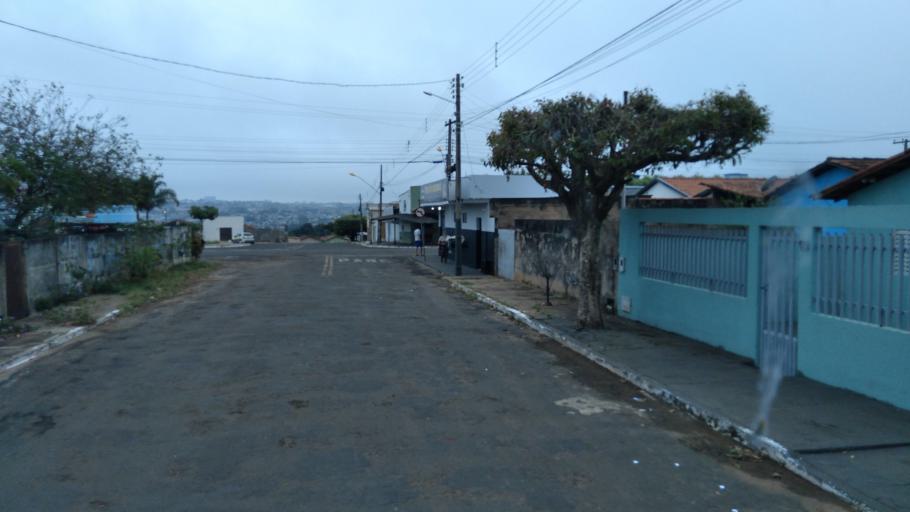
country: BR
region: Goias
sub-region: Mineiros
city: Mineiros
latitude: -17.5741
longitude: -52.5397
